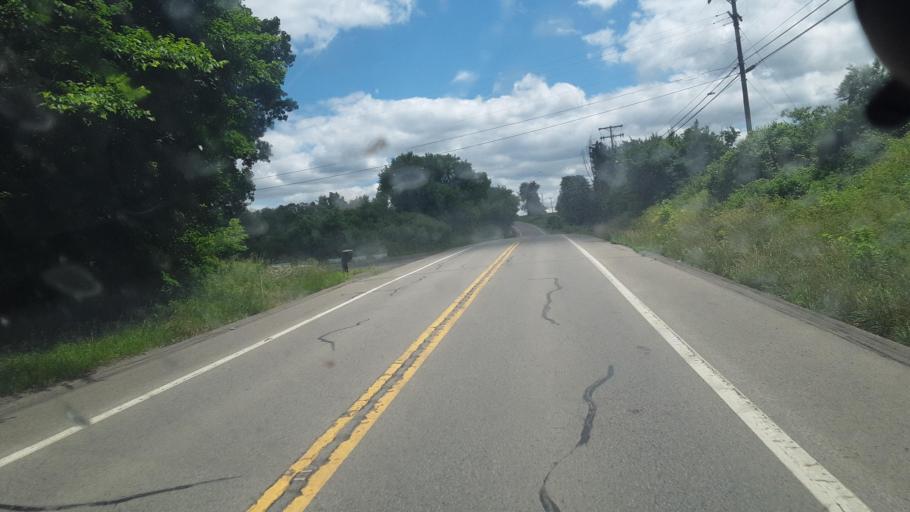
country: US
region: Pennsylvania
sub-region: Butler County
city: Slippery Rock
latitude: 40.9782
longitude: -80.1685
